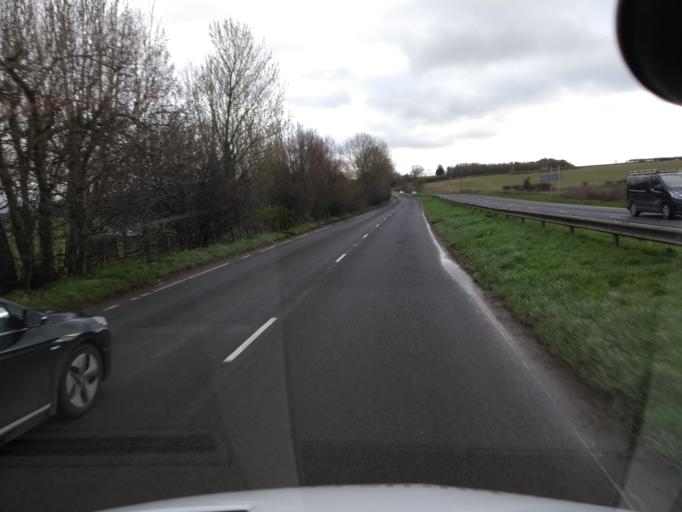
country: GB
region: England
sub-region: Somerset
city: Yeovil
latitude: 50.9445
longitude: -2.5849
